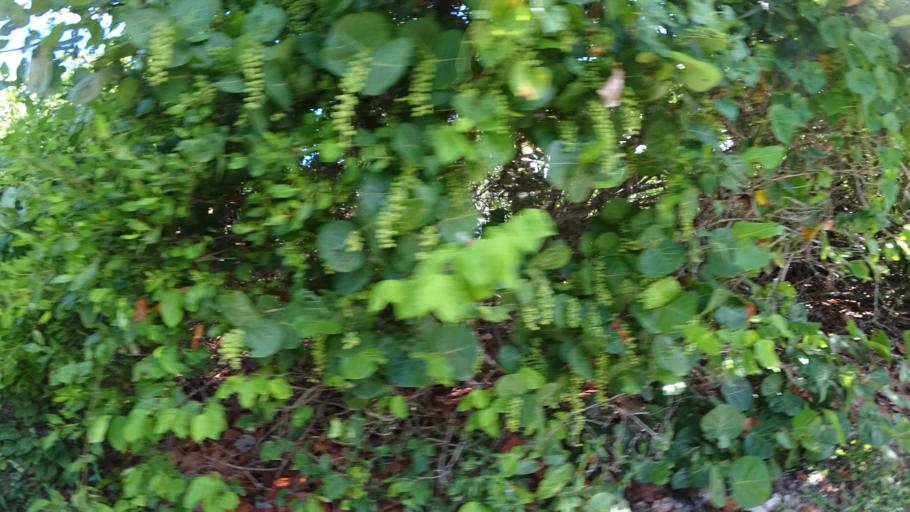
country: US
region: Florida
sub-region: Manatee County
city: Holmes Beach
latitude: 27.5200
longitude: -82.6707
